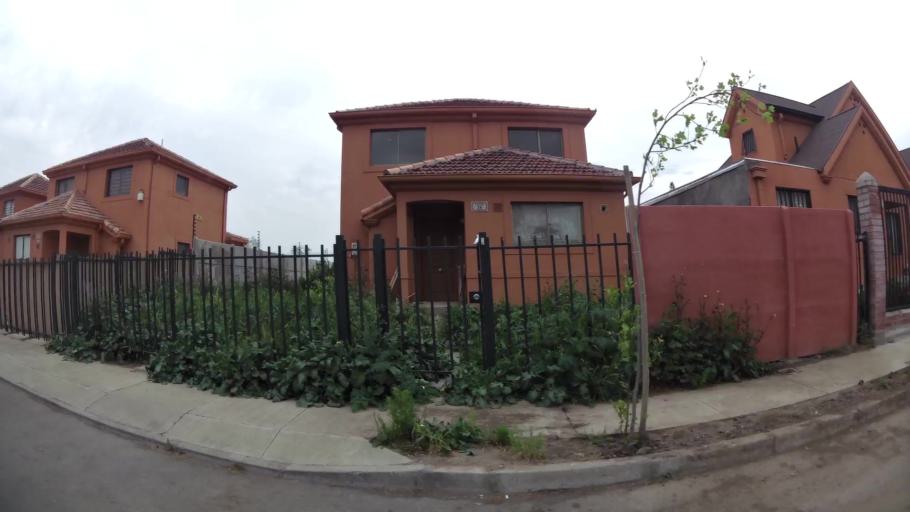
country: CL
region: Santiago Metropolitan
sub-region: Provincia de Chacabuco
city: Chicureo Abajo
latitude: -33.2160
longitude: -70.6685
